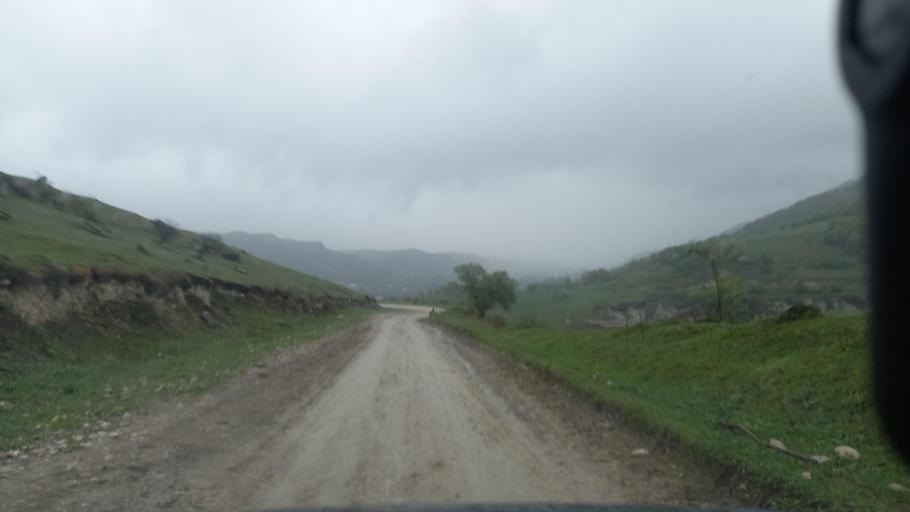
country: RU
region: Kabardino-Balkariya
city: Gundelen
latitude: 43.5958
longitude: 43.1381
